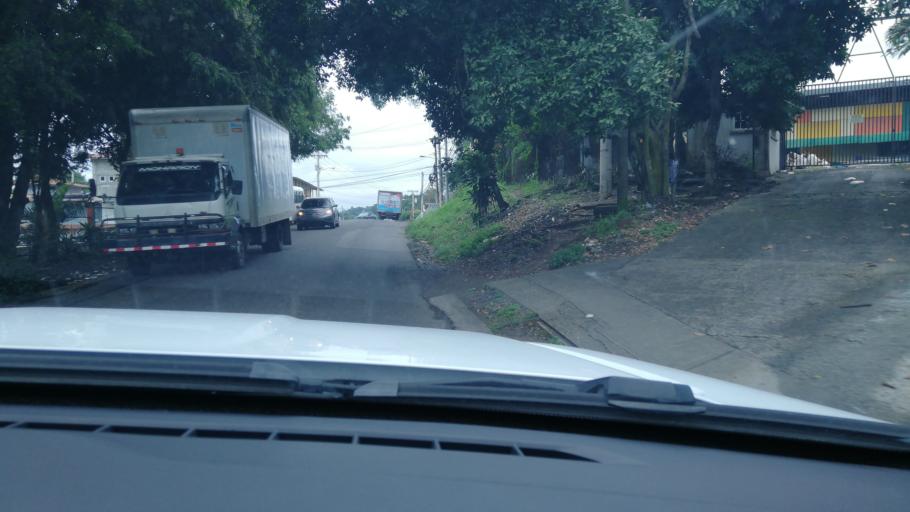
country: PA
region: Panama
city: Las Cumbres
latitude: 9.0769
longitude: -79.5240
